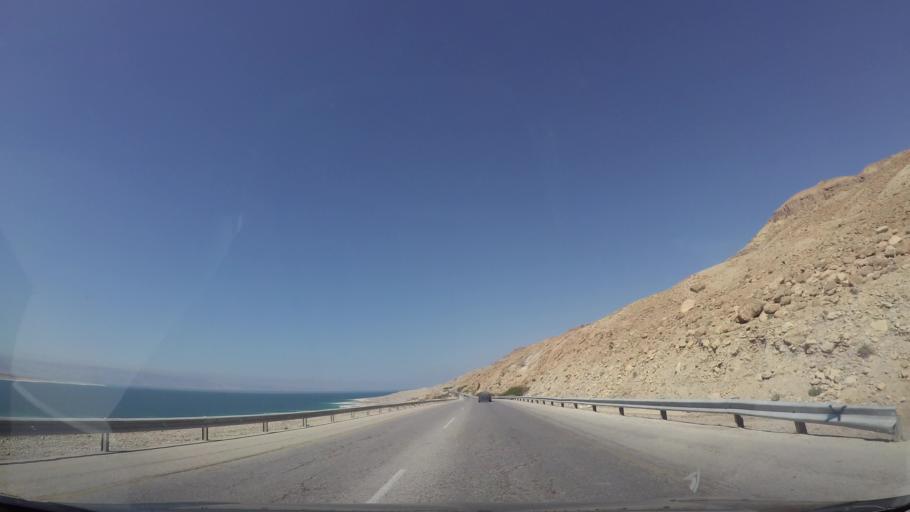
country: JO
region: Karak
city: Al Qasr
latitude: 31.3475
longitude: 35.5478
